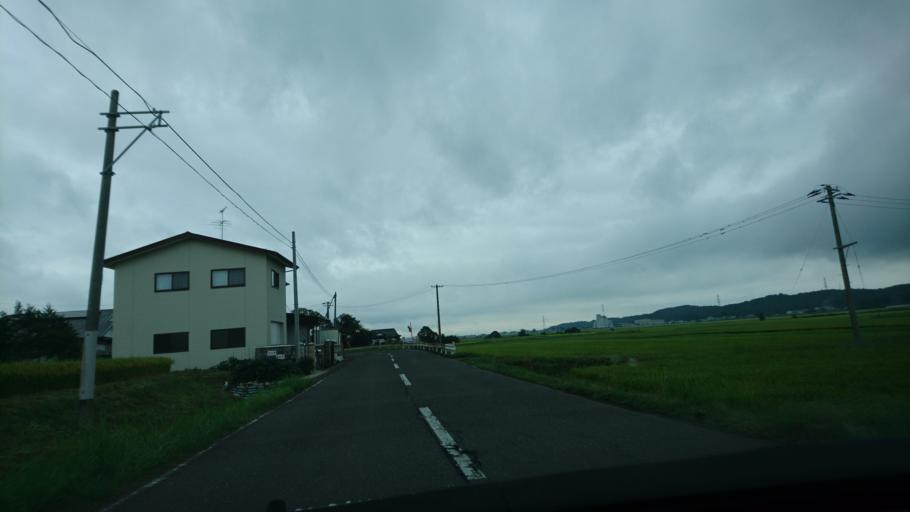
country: JP
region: Iwate
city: Ichinoseki
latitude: 38.8112
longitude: 140.9713
